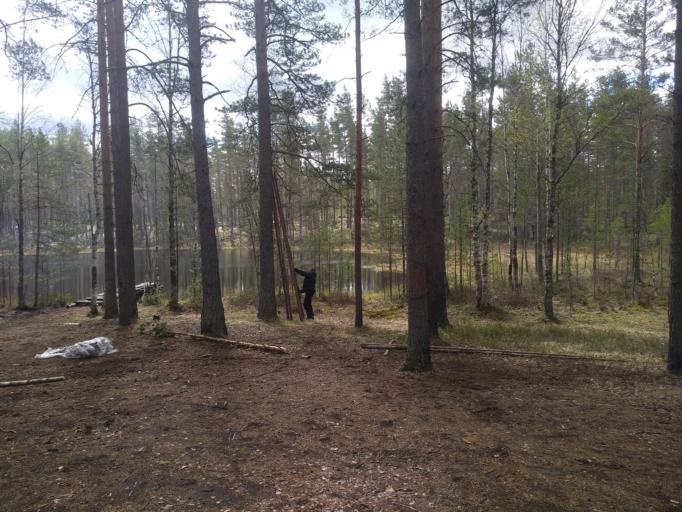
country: RU
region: Leningrad
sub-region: Vsevolzhskij Rajon
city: Vaskelovo
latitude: 60.5149
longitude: 30.4768
